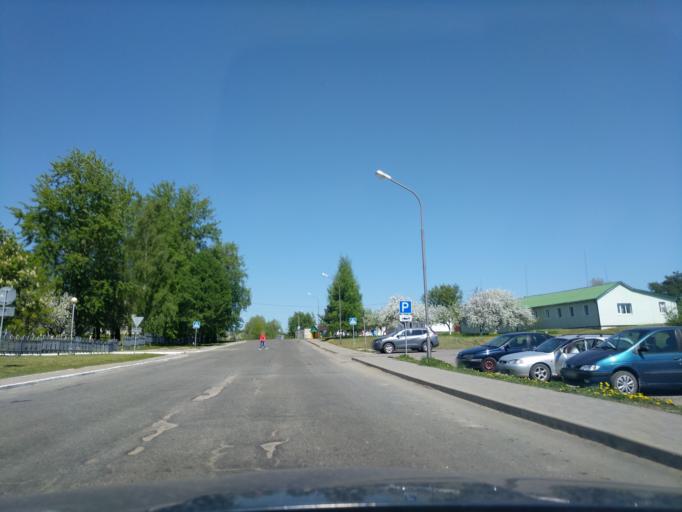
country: BY
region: Minsk
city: Myadzyel
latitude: 54.8871
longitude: 26.9156
